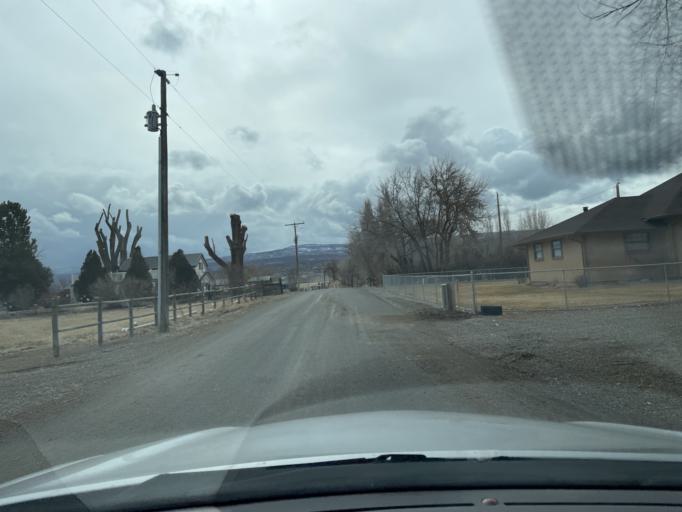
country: US
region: Colorado
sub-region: Mesa County
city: Loma
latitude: 39.1829
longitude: -108.8037
